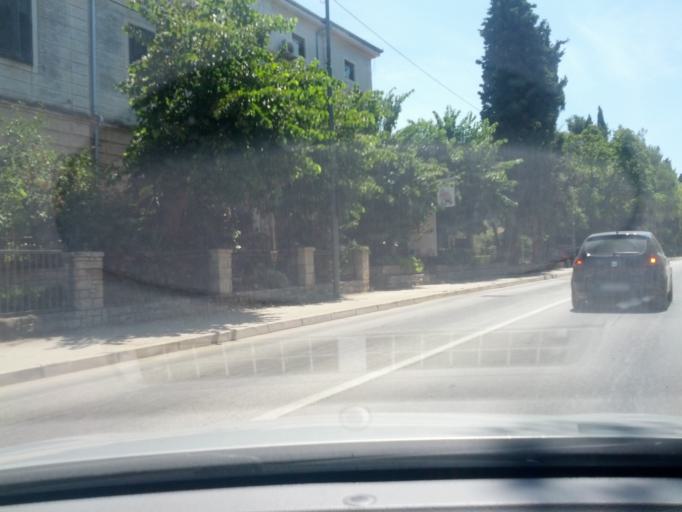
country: HR
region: Istarska
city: Fazana
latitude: 44.9258
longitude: 13.8048
